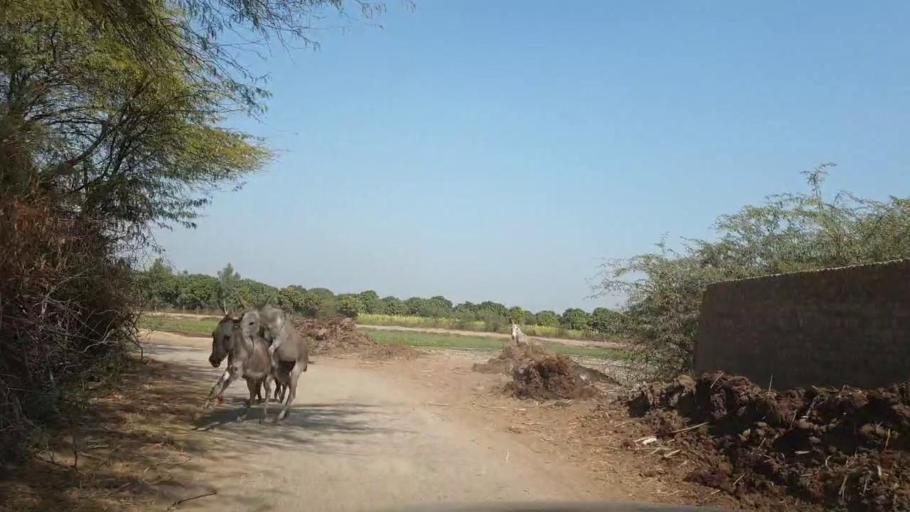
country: PK
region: Sindh
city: Tando Allahyar
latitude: 25.5647
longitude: 68.7082
